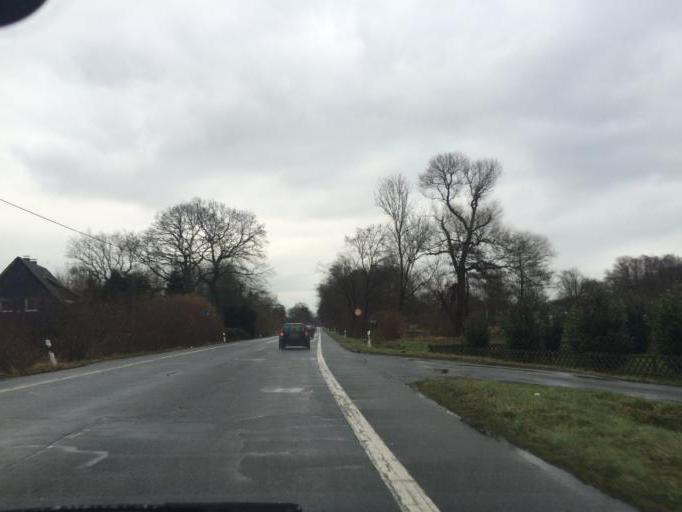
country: DE
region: North Rhine-Westphalia
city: Dorsten
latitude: 51.6424
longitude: 6.9592
